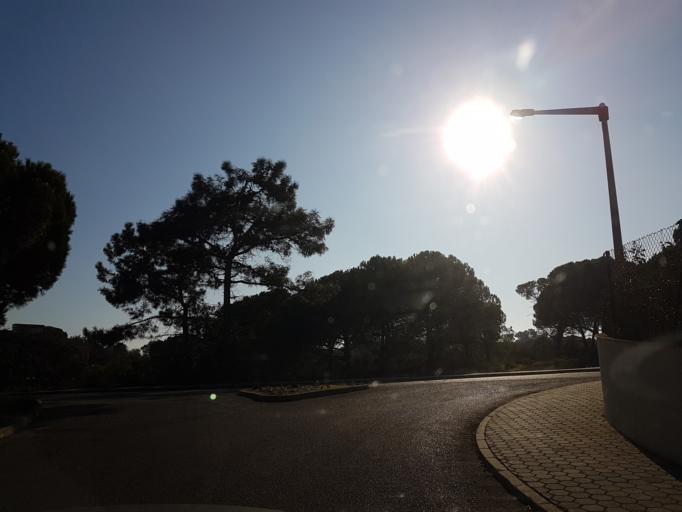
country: PT
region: Faro
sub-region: Albufeira
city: Albufeira
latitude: 37.0949
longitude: -8.2017
